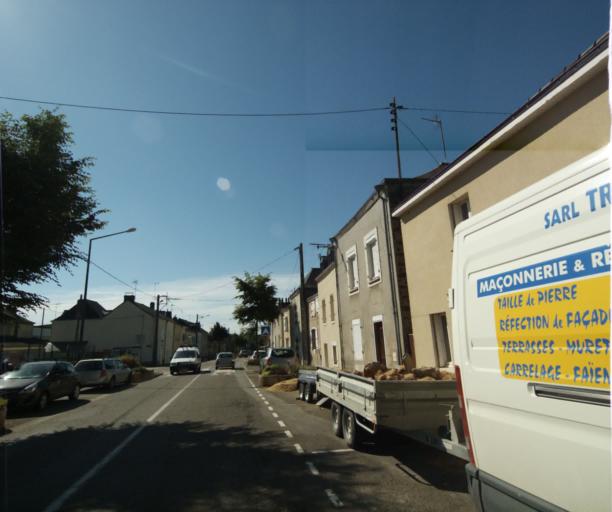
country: FR
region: Pays de la Loire
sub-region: Departement de la Mayenne
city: Laval
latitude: 48.0509
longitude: -0.7473
